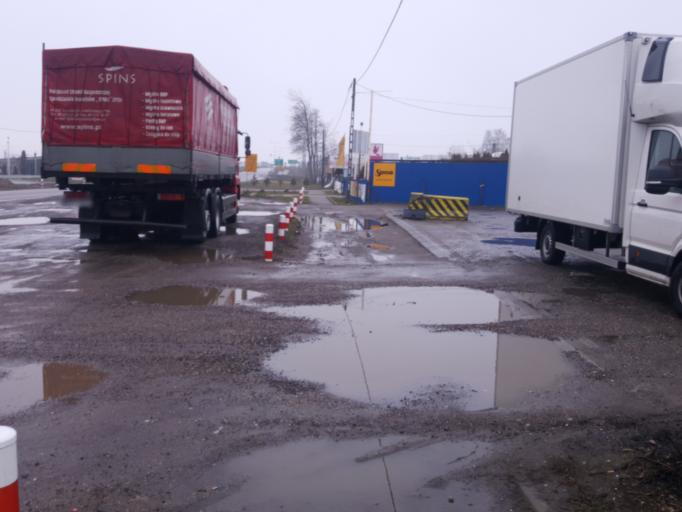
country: PL
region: Masovian Voivodeship
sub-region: Powiat ostrowski
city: Ostrow Mazowiecka
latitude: 52.8216
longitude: 21.8875
